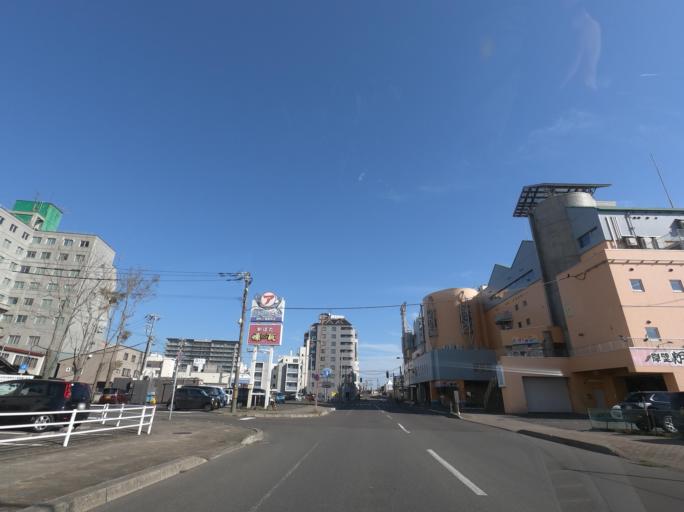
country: JP
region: Hokkaido
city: Kushiro
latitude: 42.9821
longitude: 144.3823
